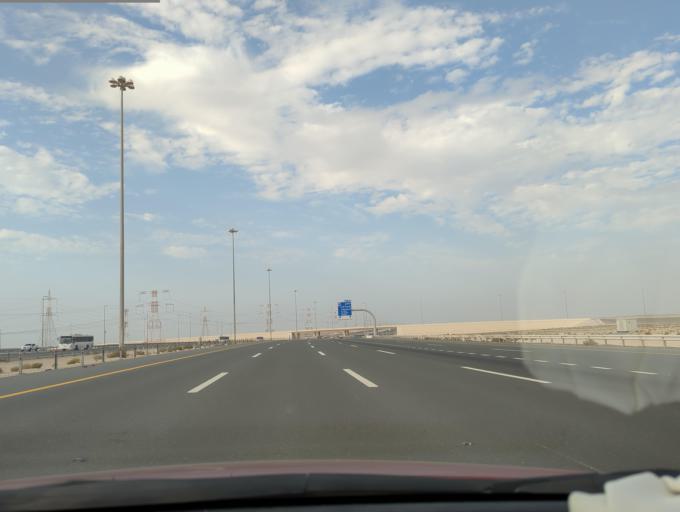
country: AE
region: Abu Dhabi
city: Abu Dhabi
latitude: 24.4549
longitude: 54.7503
